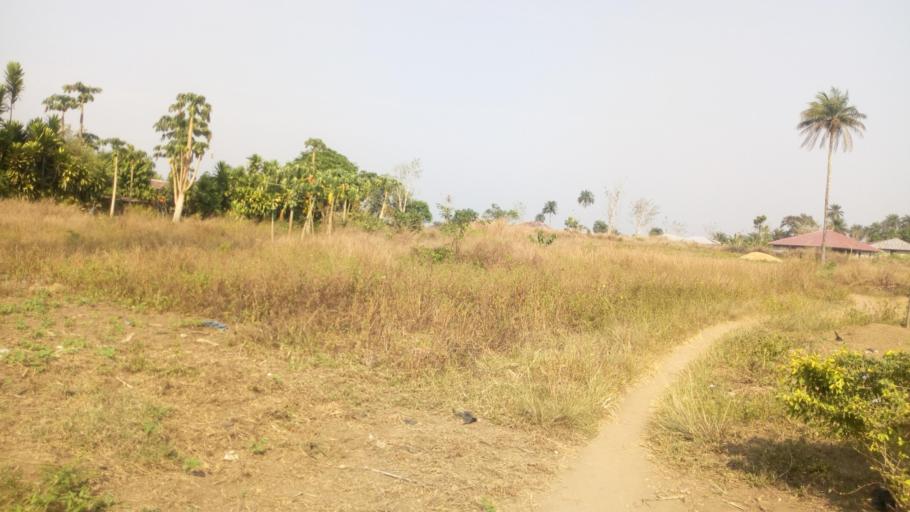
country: SL
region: Southern Province
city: Mogbwemo
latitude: 7.6159
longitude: -12.1773
